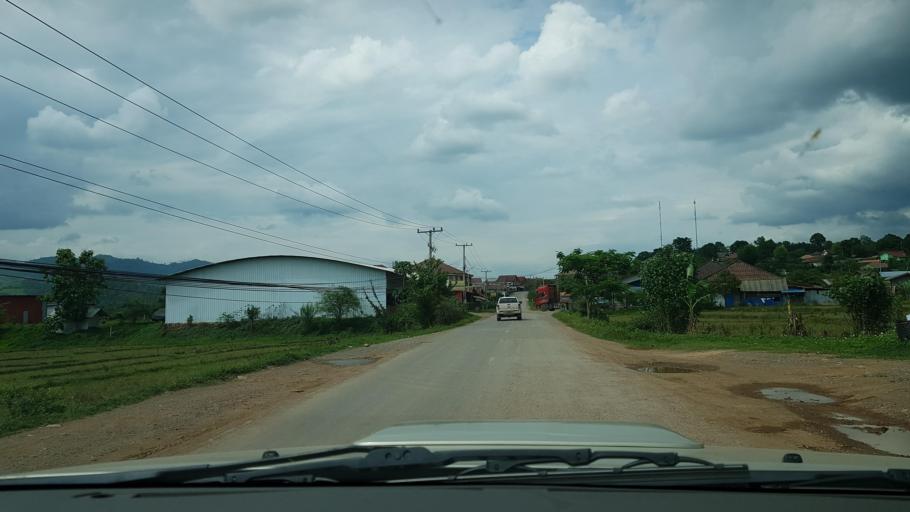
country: LA
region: Loungnamtha
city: Muang Nale
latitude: 20.2953
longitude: 101.6347
